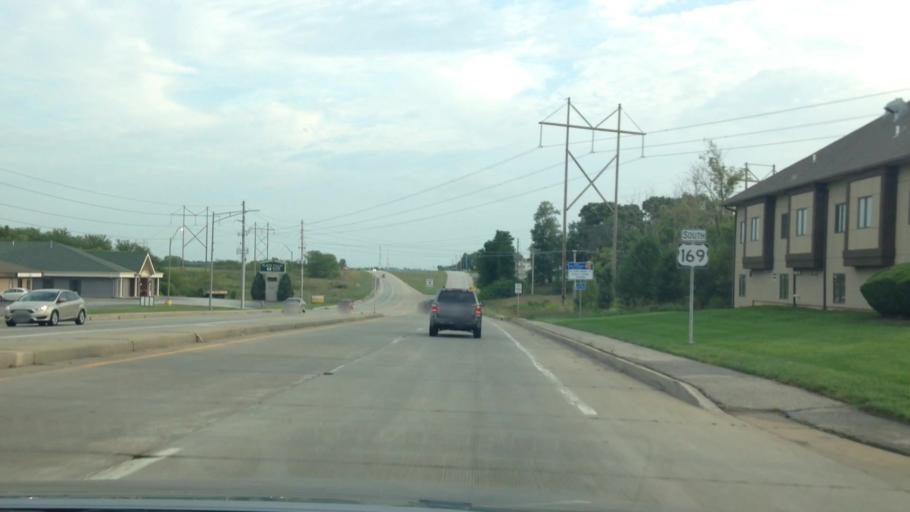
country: US
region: Missouri
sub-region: Clay County
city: Smithville
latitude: 39.3615
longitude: -94.5839
